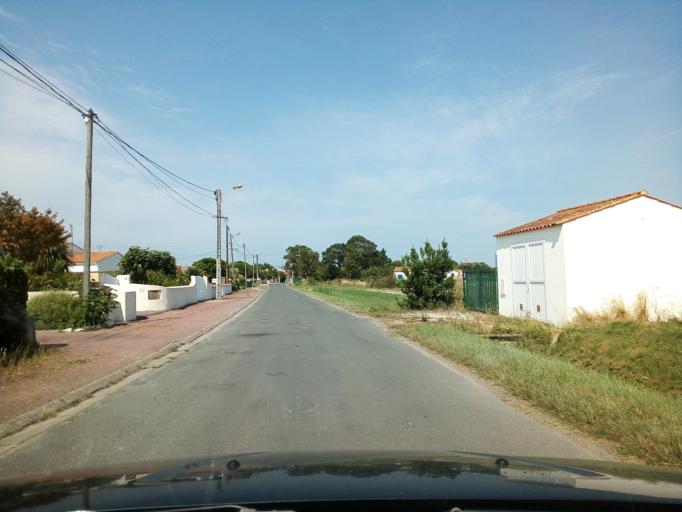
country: FR
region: Poitou-Charentes
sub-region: Departement de la Charente-Maritime
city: Dolus-d'Oleron
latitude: 45.9480
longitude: -1.2982
